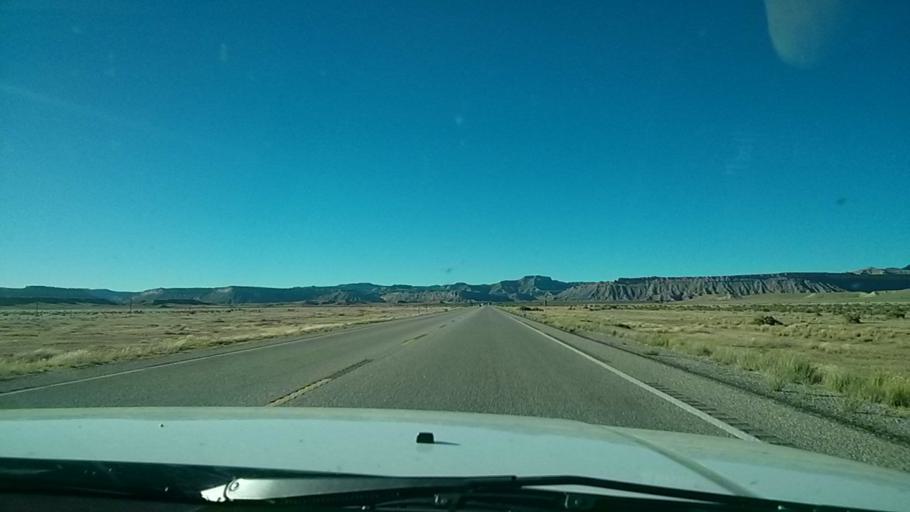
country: US
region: Utah
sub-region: Grand County
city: Moab
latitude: 38.9231
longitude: -109.8154
